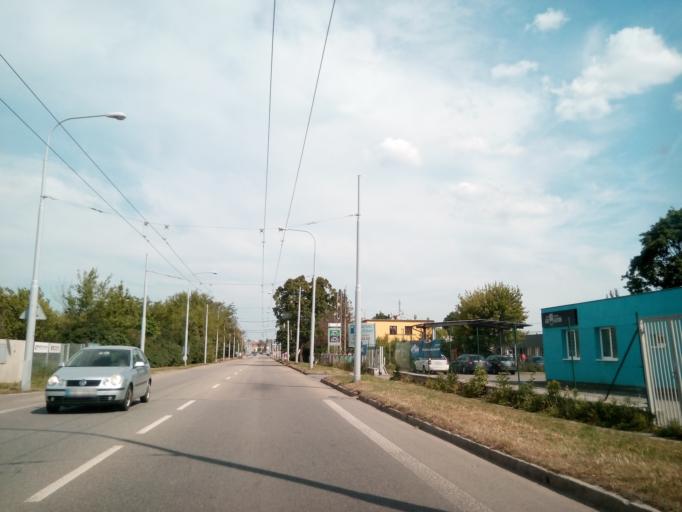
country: CZ
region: South Moravian
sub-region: Mesto Brno
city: Brno
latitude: 49.1849
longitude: 16.6597
